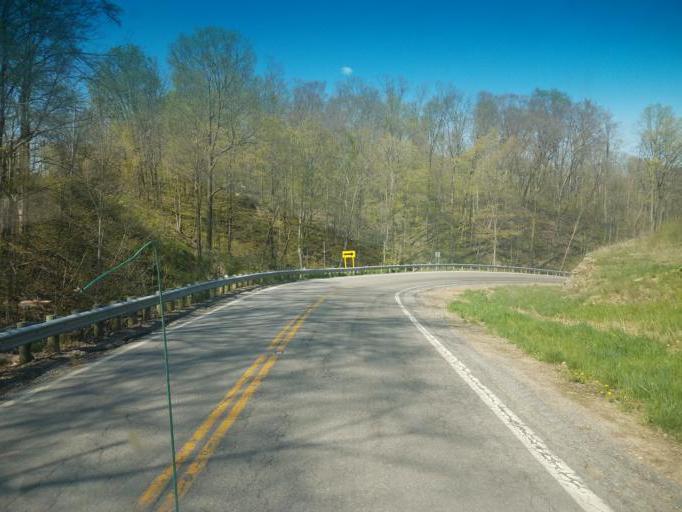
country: US
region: Ohio
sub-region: Wayne County
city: West Salem
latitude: 40.9363
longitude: -82.0209
